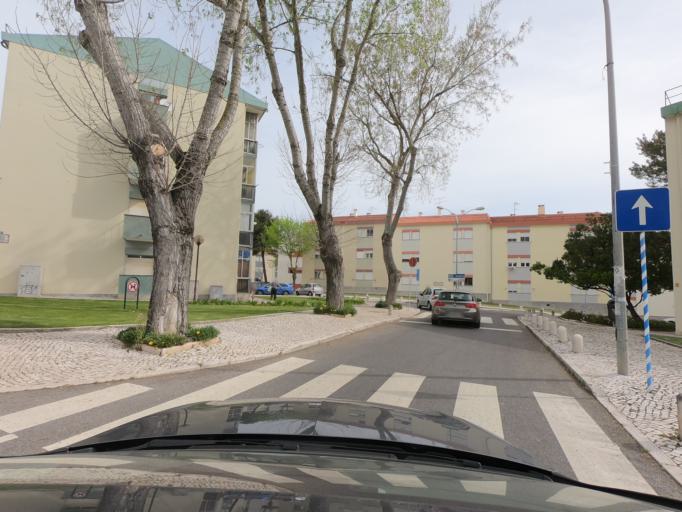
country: PT
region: Lisbon
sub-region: Oeiras
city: Porto Salvo
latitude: 38.7160
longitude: -9.3014
